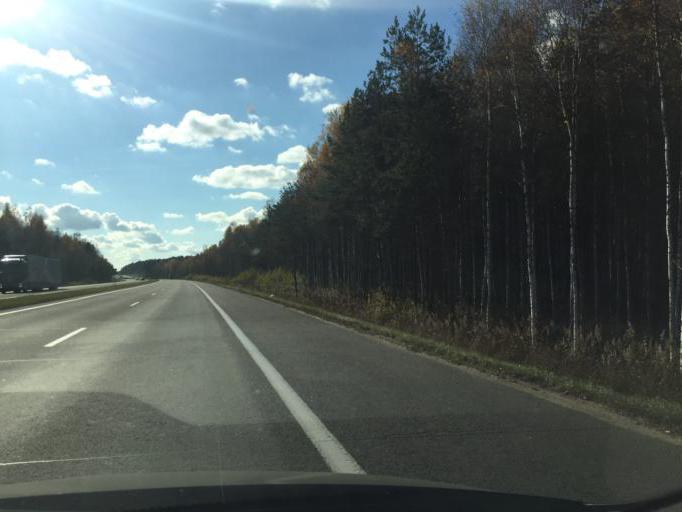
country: BY
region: Minsk
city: Slabada
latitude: 53.9378
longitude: 27.9637
